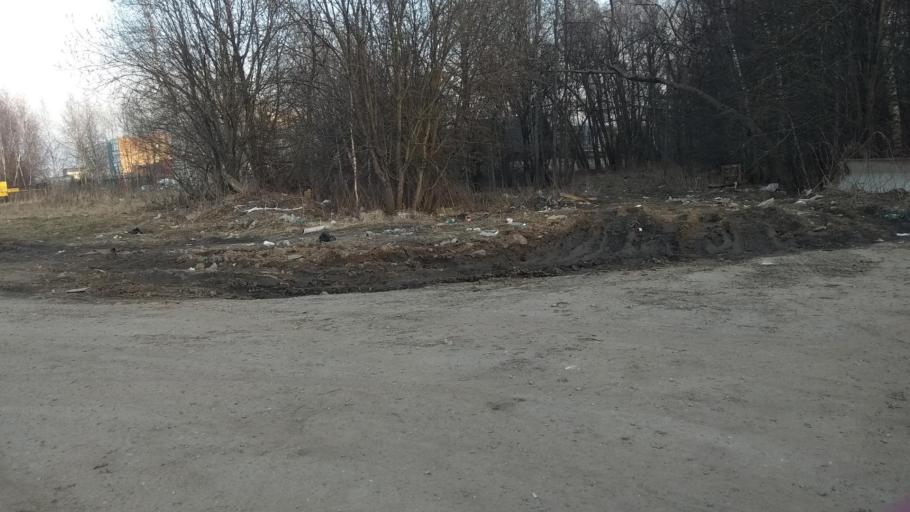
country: RU
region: Moskovskaya
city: Razvilka
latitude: 55.5635
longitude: 37.7452
